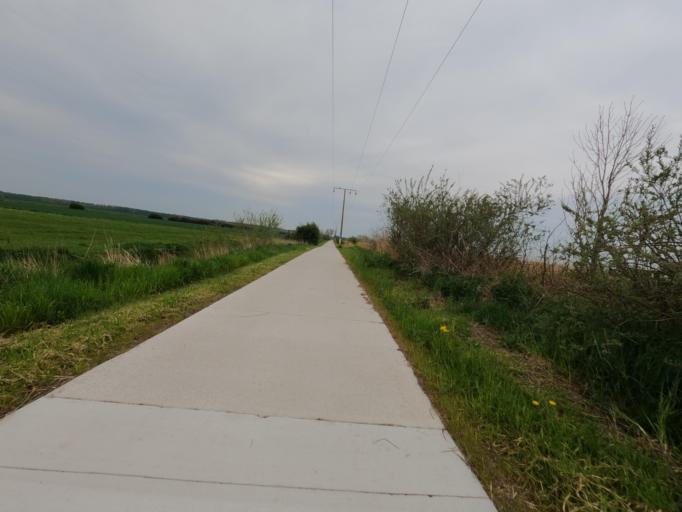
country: DE
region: Mecklenburg-Vorpommern
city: Saal
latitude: 54.3044
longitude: 12.4992
